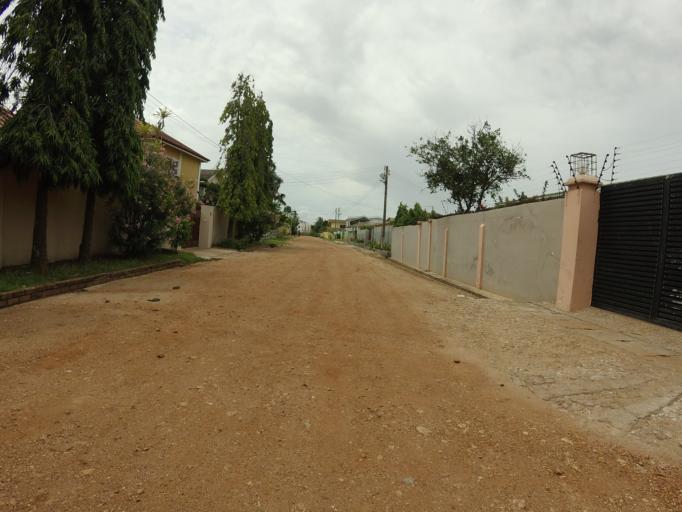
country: GH
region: Greater Accra
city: Accra
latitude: 5.6024
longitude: -0.2115
